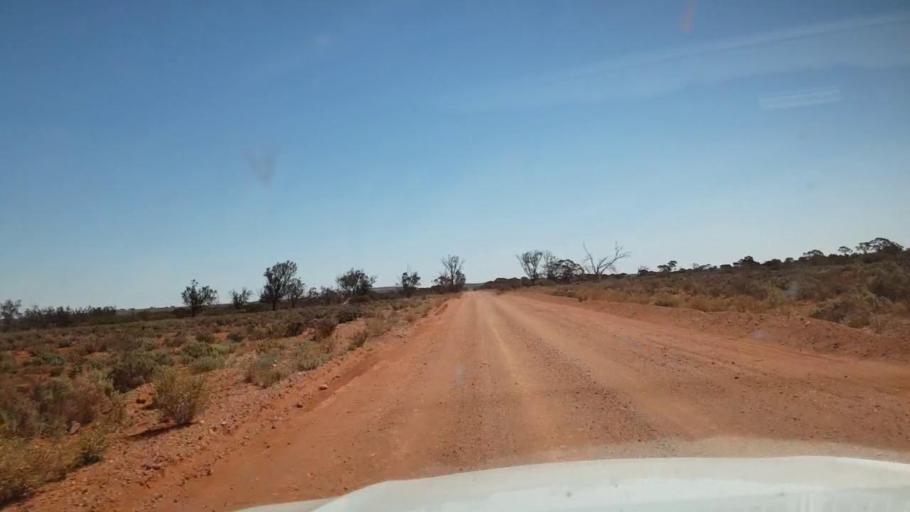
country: AU
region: South Australia
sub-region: Whyalla
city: Whyalla
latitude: -32.6844
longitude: 137.1031
